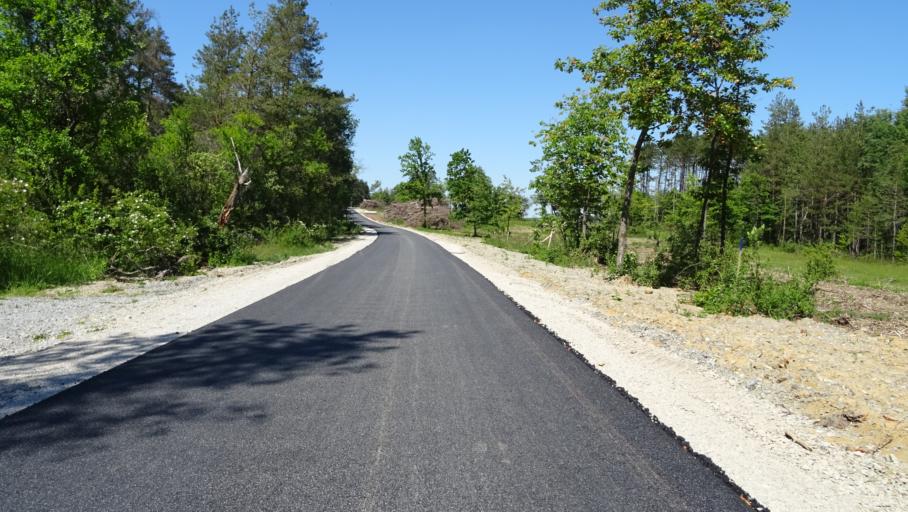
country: DE
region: Baden-Wuerttemberg
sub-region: Karlsruhe Region
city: Buchen
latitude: 49.4882
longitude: 9.3291
